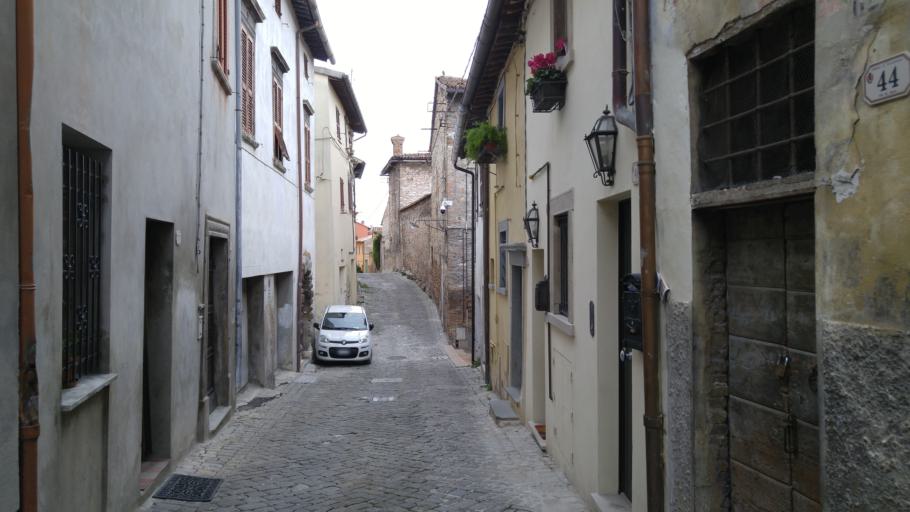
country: IT
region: The Marches
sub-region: Provincia di Pesaro e Urbino
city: Fossombrone
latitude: 43.6900
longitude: 12.8077
